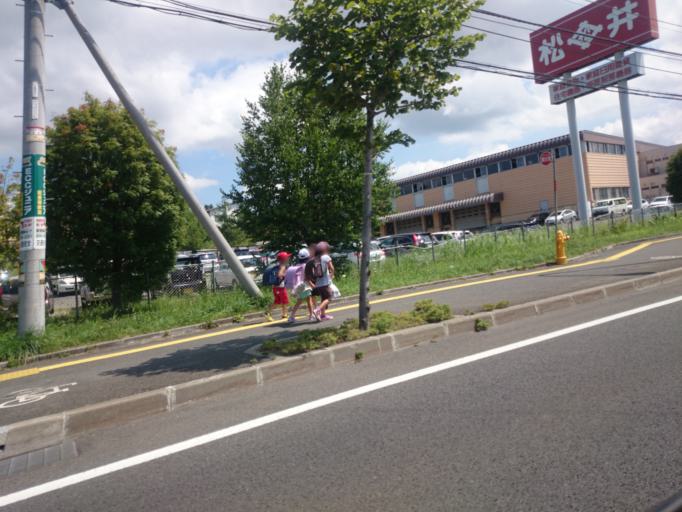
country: JP
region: Hokkaido
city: Ebetsu
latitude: 43.0543
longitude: 141.4856
